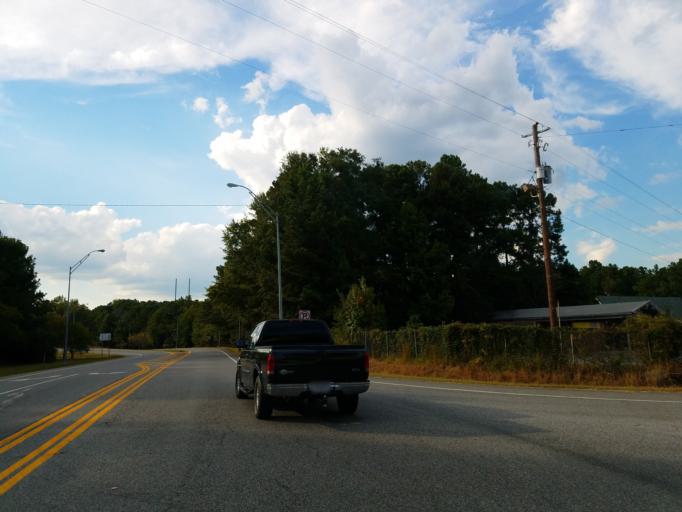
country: US
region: Georgia
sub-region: Monroe County
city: Forsyth
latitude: 33.0552
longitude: -83.9507
